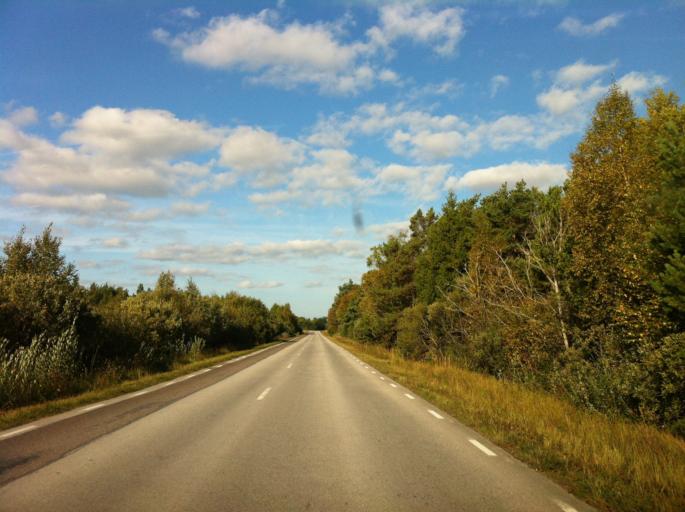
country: SE
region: Gotland
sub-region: Gotland
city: Slite
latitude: 57.4416
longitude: 18.7331
